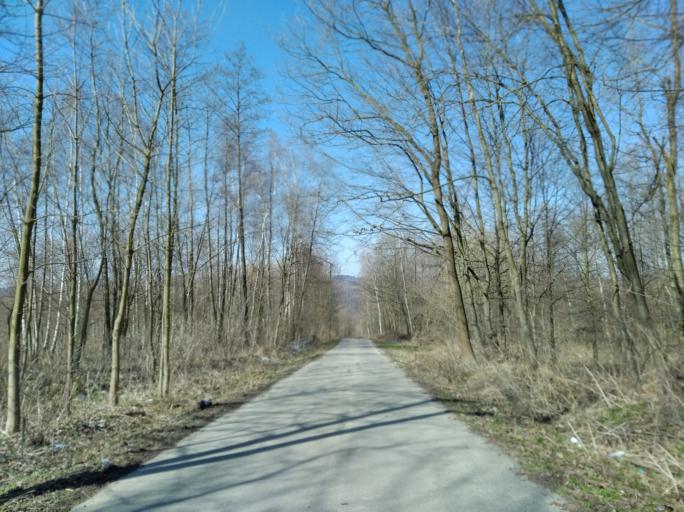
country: PL
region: Subcarpathian Voivodeship
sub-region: Powiat strzyzowski
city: Strzyzow
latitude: 49.8681
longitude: 21.8311
